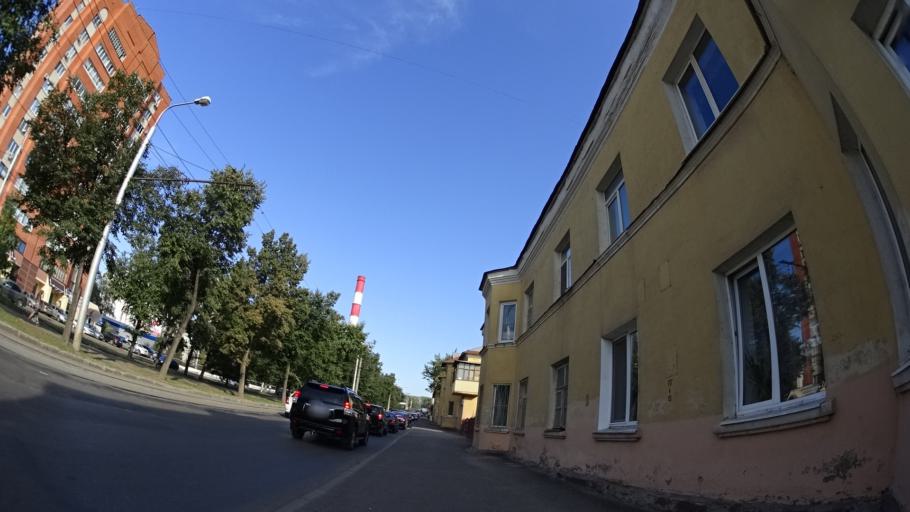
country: RU
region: Bashkortostan
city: Ufa
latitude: 54.7411
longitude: 55.9637
